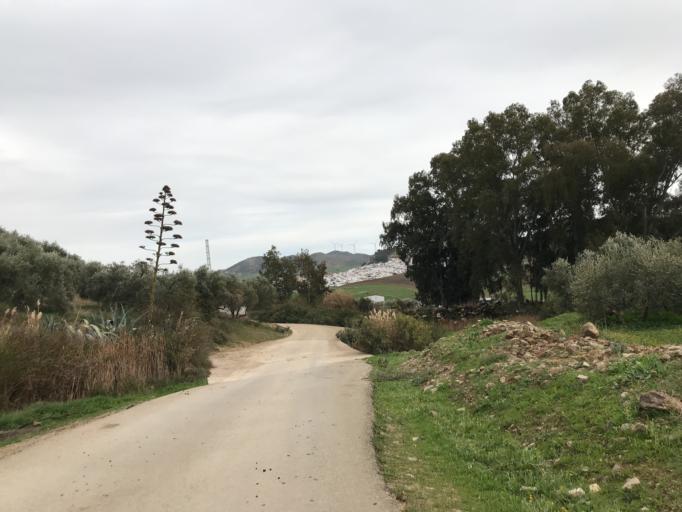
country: ES
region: Andalusia
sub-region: Provincia de Malaga
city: Ardales
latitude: 36.8831
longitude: -4.8569
